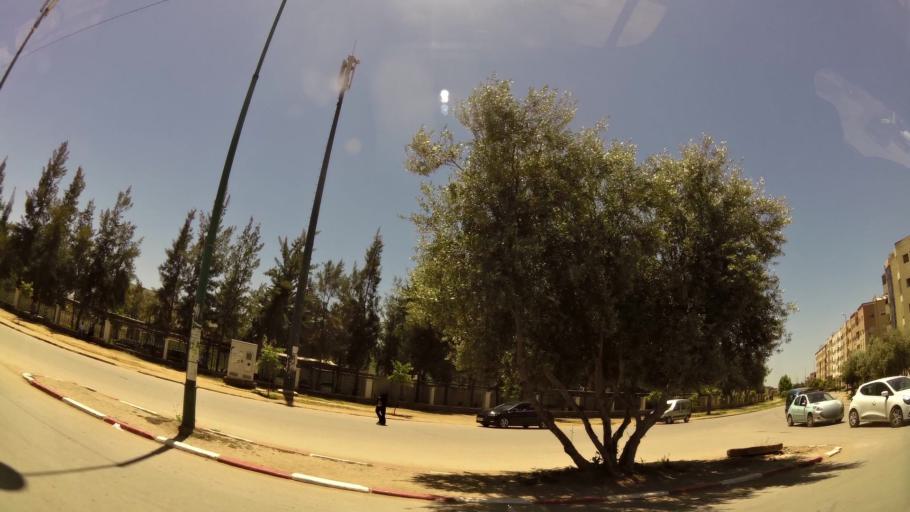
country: MA
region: Meknes-Tafilalet
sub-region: Meknes
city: Meknes
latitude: 33.8589
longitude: -5.5718
